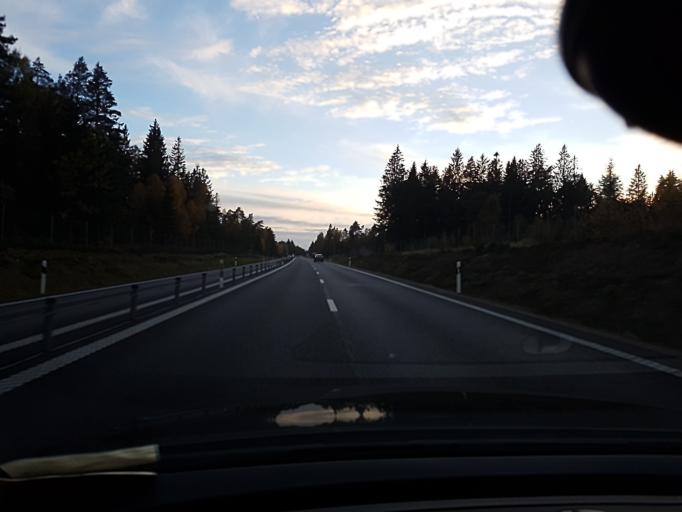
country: SE
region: Kronoberg
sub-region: Ljungby Kommun
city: Ljungby
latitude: 56.7815
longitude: 13.8204
